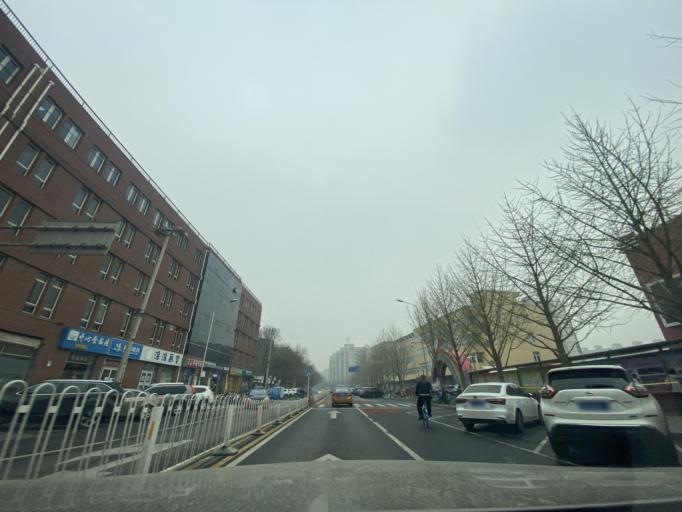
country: CN
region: Beijing
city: Sijiqing
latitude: 39.9651
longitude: 116.2714
